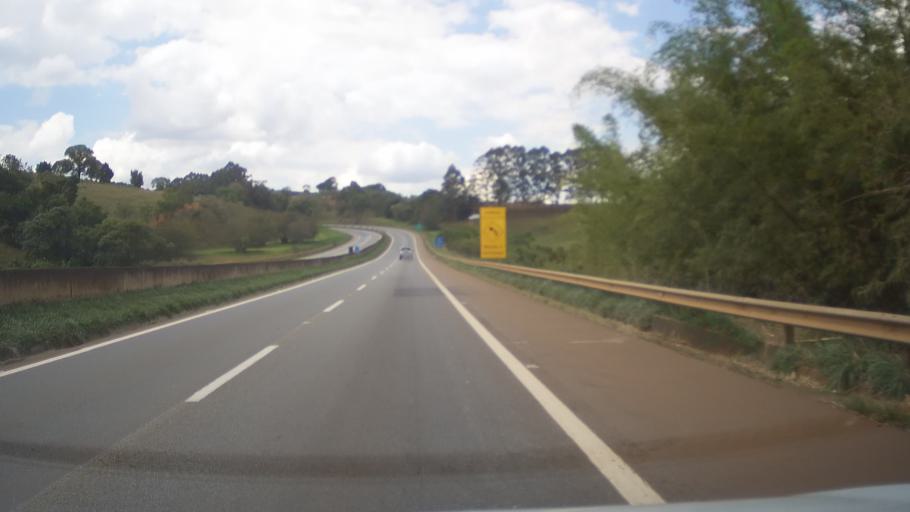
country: BR
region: Minas Gerais
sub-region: Nepomuceno
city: Nepomuceno
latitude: -21.2750
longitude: -45.1379
